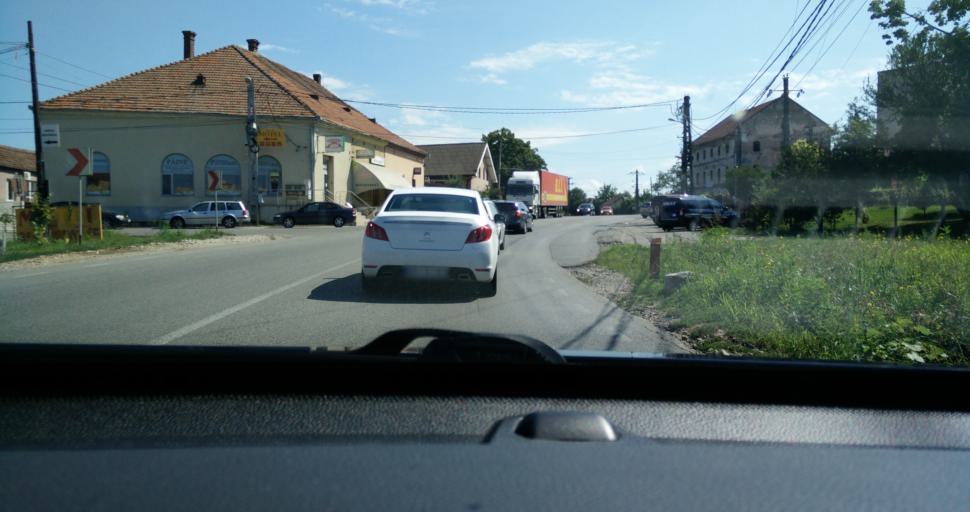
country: RO
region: Bihor
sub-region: Comuna Osorheiu
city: Alparea
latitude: 47.0409
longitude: 22.0269
